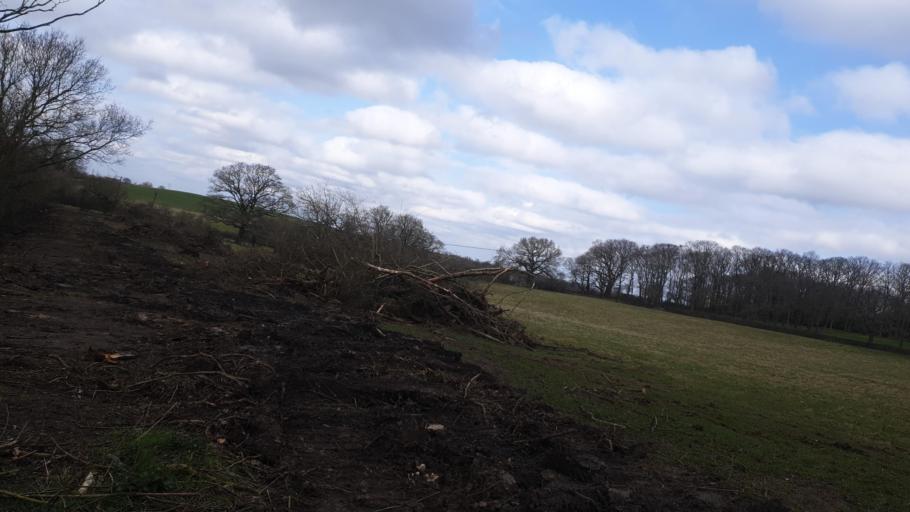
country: GB
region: England
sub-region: Oxfordshire
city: Boars Hill
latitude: 51.7181
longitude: -1.2828
